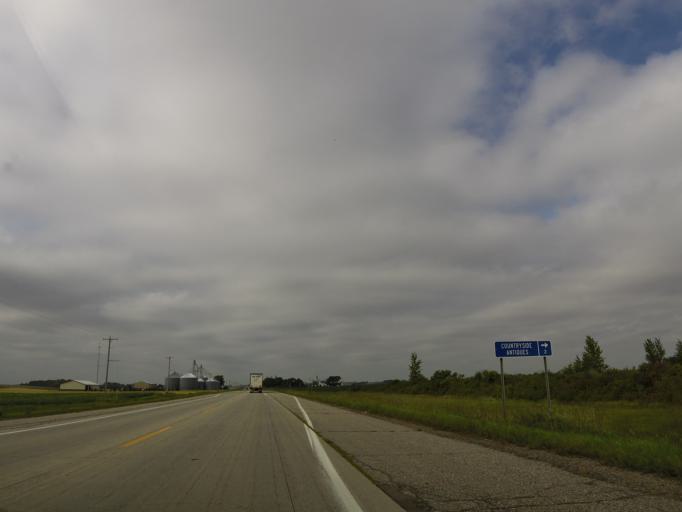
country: US
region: Minnesota
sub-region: Renville County
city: Bird Island
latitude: 44.7676
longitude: -94.9133
